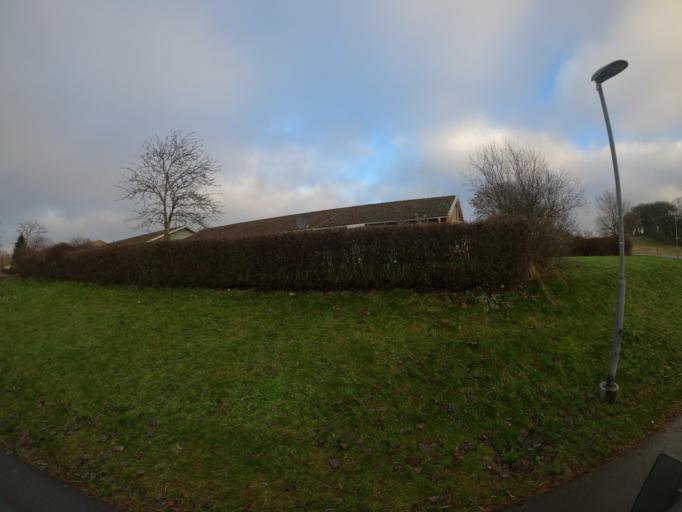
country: SE
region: Skane
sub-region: Svedala Kommun
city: Svedala
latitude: 55.5165
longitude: 13.2168
